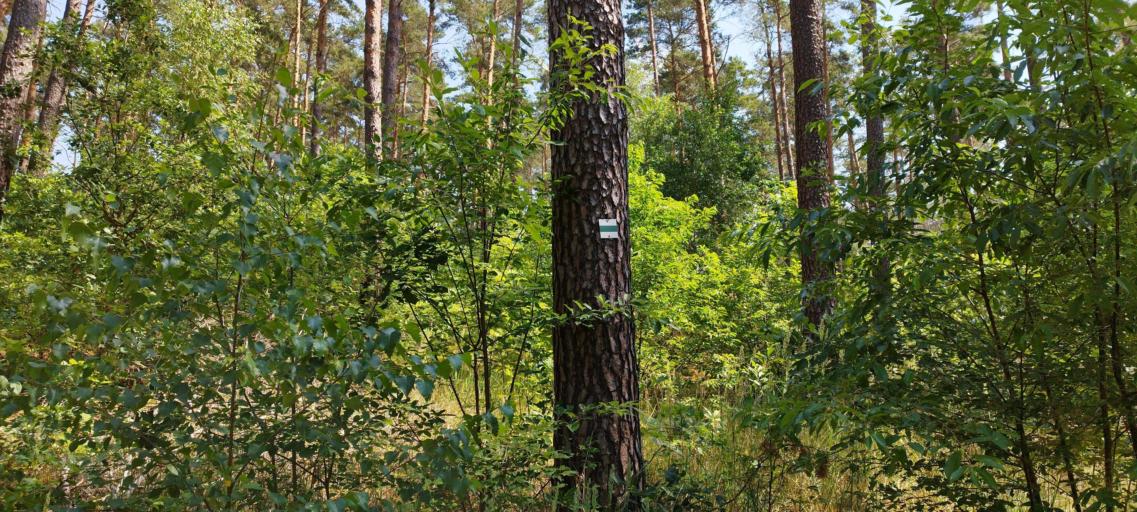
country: DE
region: Brandenburg
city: Langewahl
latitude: 52.3158
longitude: 14.1020
